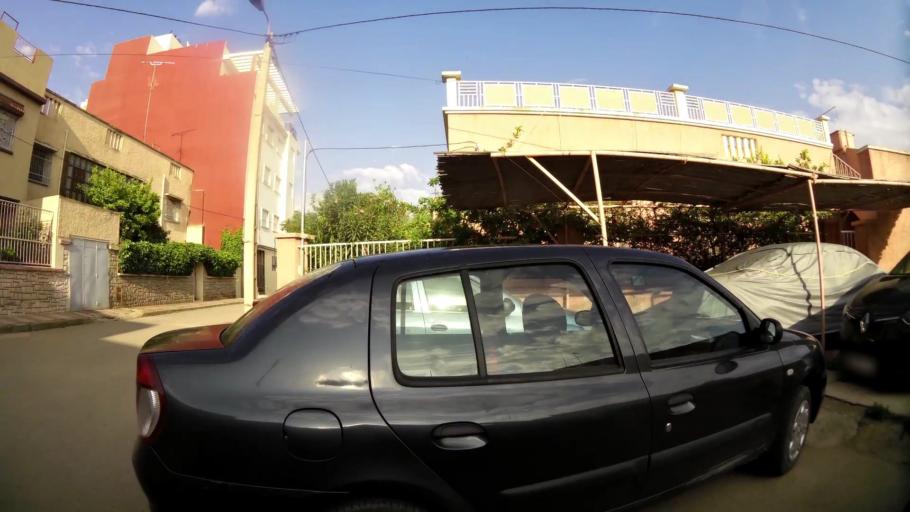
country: MA
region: Oriental
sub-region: Oujda-Angad
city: Oujda
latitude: 34.6729
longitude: -1.9237
